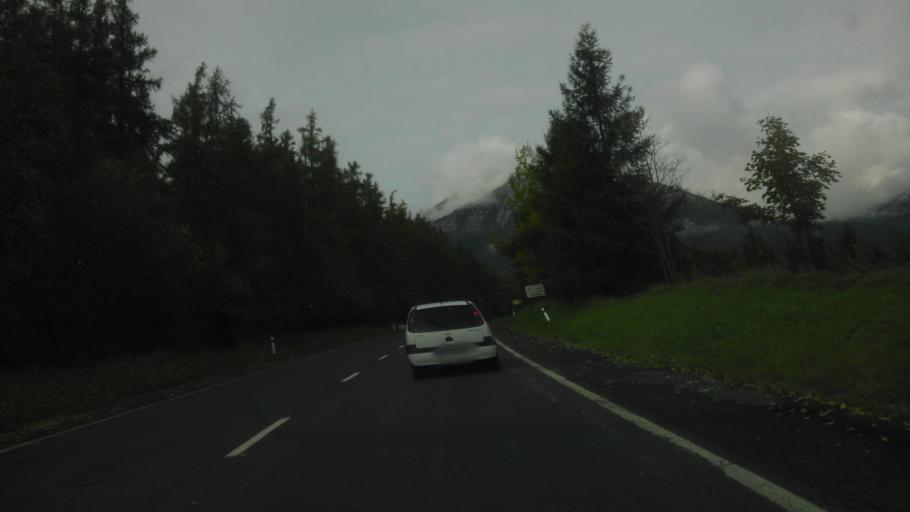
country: SK
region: Presovsky
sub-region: Okres Poprad
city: Nova Lesna
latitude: 49.1182
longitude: 20.2540
